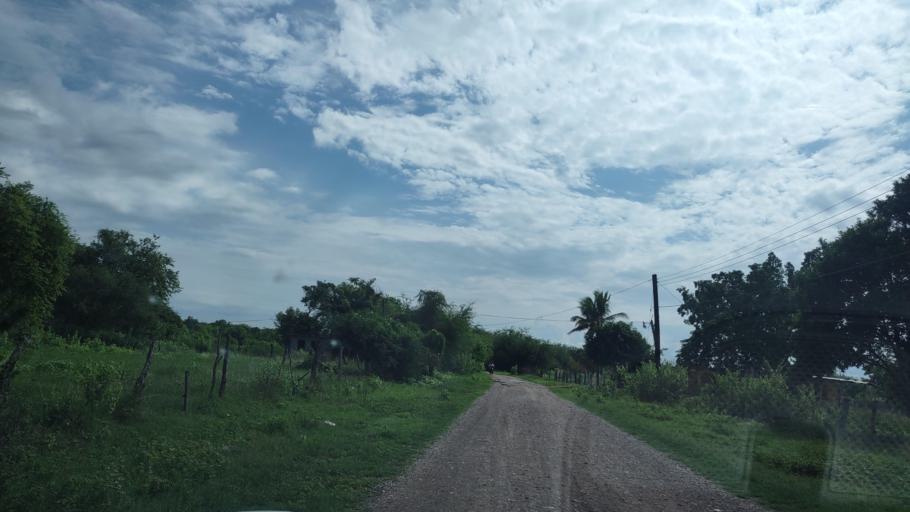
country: MX
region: Veracruz
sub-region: Panuco
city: Oviedo
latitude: 22.0012
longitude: -98.4589
